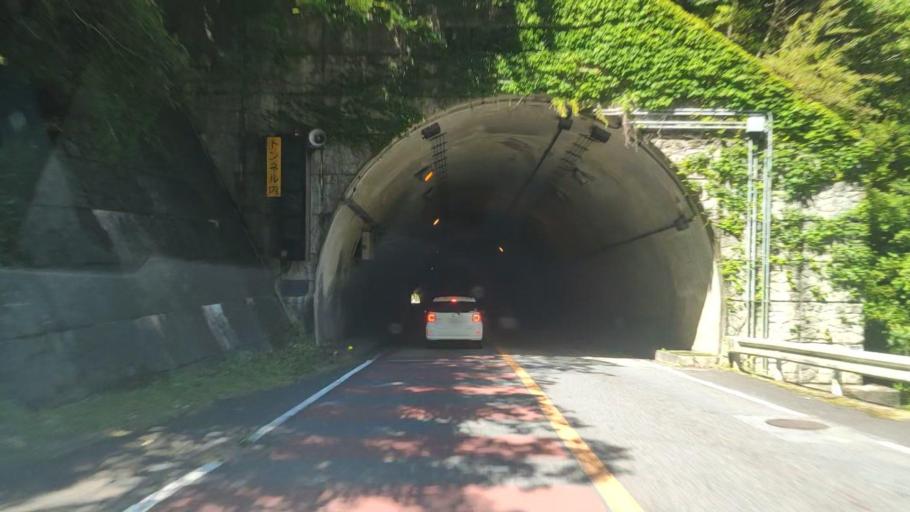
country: JP
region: Nara
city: Yoshino-cho
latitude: 34.2609
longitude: 136.0027
